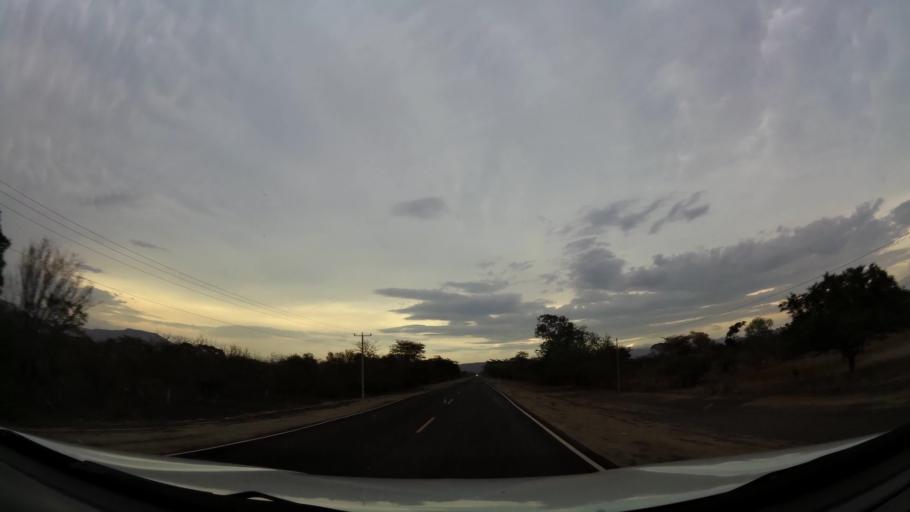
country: NI
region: Matagalpa
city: Ciudad Dario
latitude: 12.8745
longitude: -86.1924
